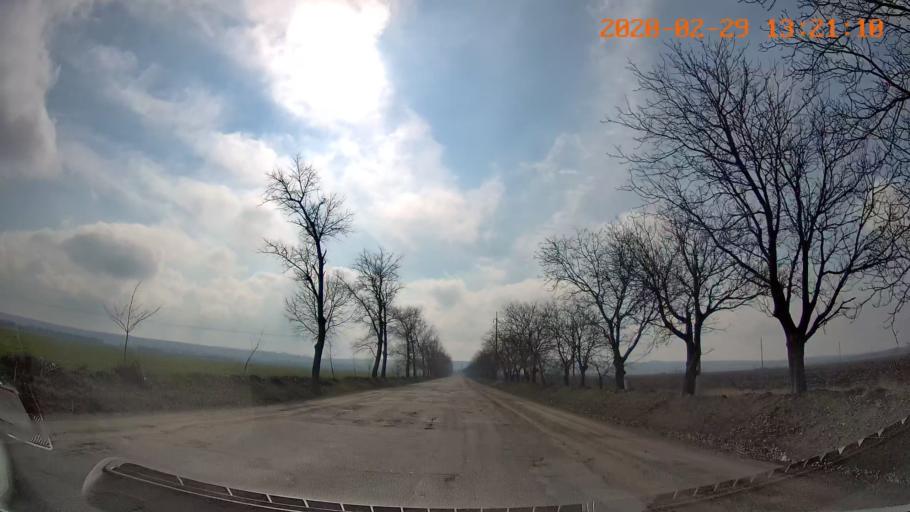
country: MD
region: Telenesti
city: Camenca
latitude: 47.9726
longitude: 28.6353
